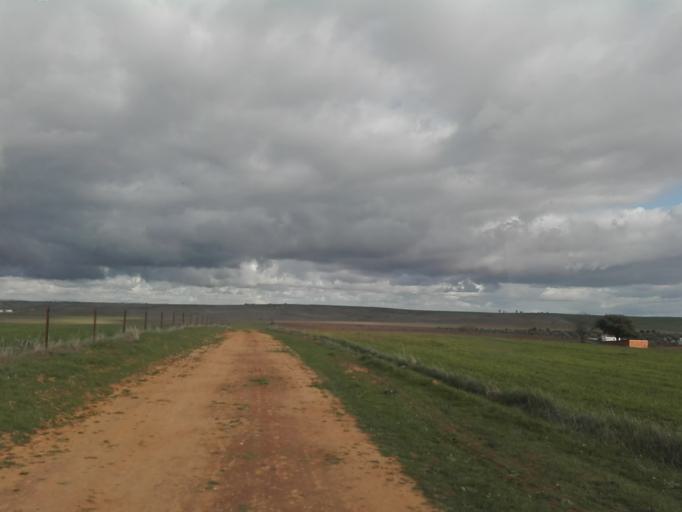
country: ES
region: Extremadura
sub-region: Provincia de Badajoz
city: Llerena
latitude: 38.2888
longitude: -6.0095
